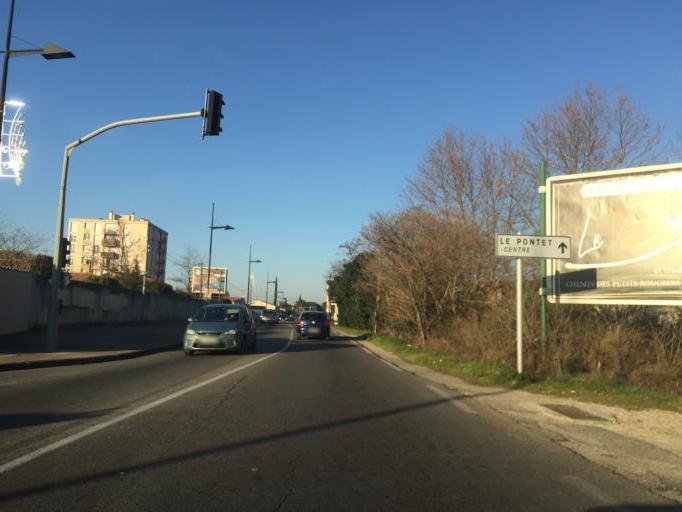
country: FR
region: Provence-Alpes-Cote d'Azur
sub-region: Departement du Vaucluse
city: Le Pontet
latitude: 43.9544
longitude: 4.8584
